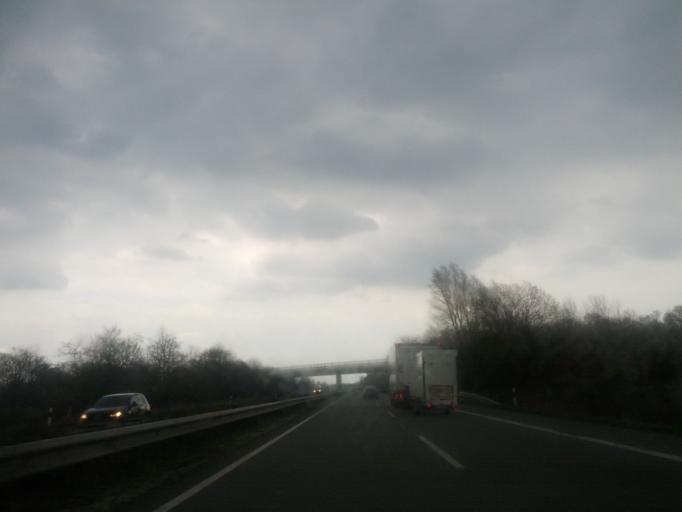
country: DE
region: Lower Saxony
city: Filsum
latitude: 53.2467
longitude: 7.6679
